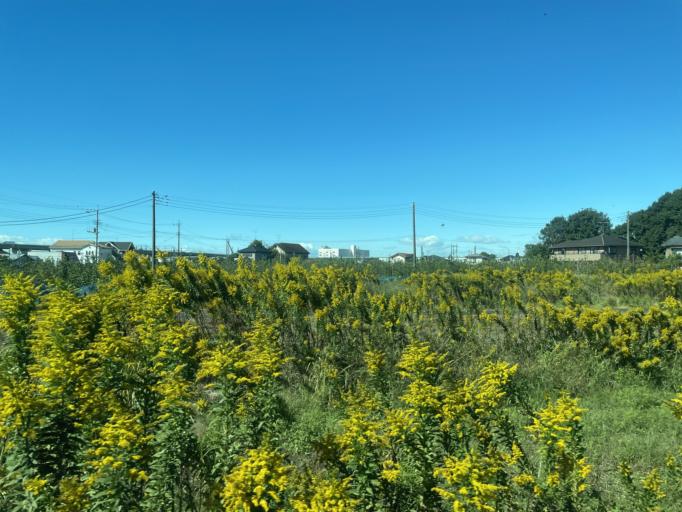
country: JP
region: Saitama
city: Kukichuo
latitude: 36.0486
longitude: 139.6735
